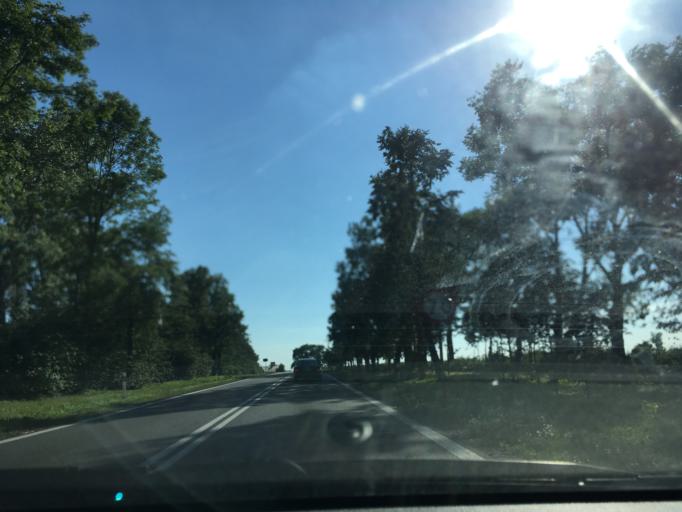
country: PL
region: Podlasie
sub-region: Powiat sokolski
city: Suchowola
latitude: 53.5121
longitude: 23.1024
